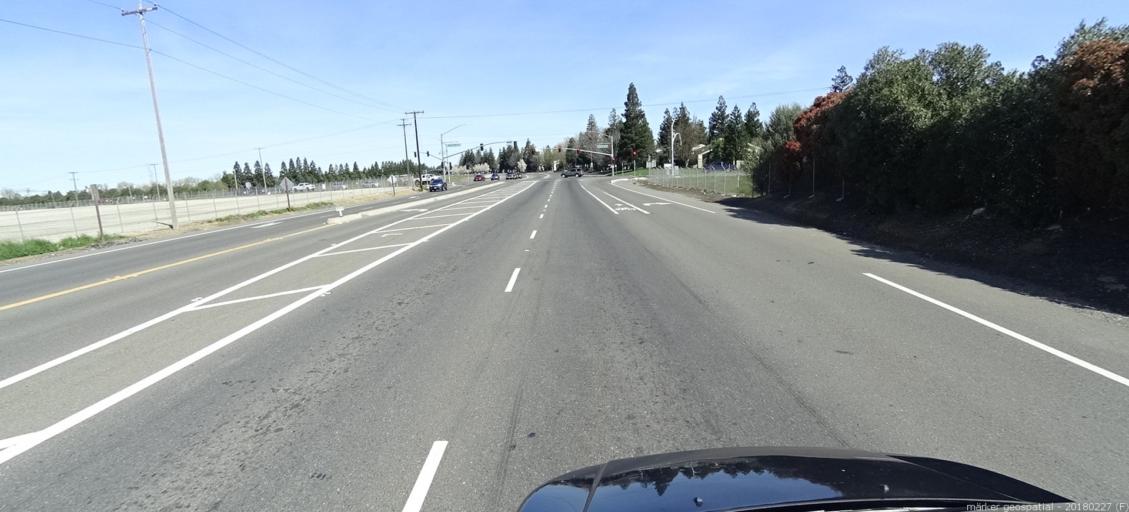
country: US
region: California
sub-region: Sacramento County
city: Rosemont
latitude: 38.5377
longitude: -121.3709
